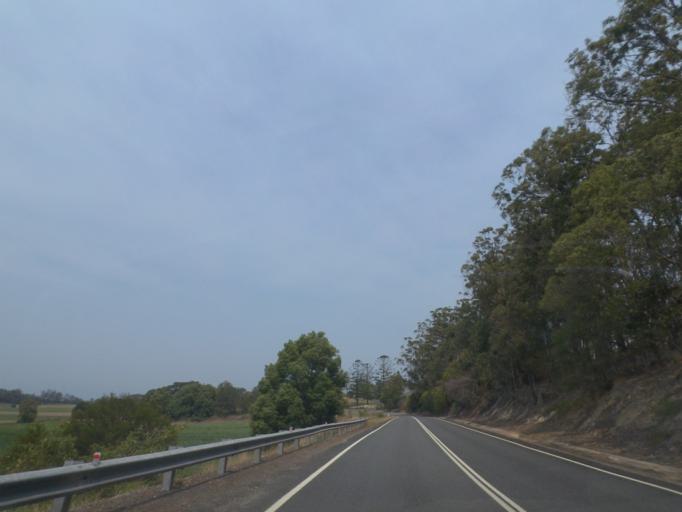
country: AU
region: New South Wales
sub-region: Tweed
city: Burringbar
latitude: -28.4580
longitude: 153.5220
